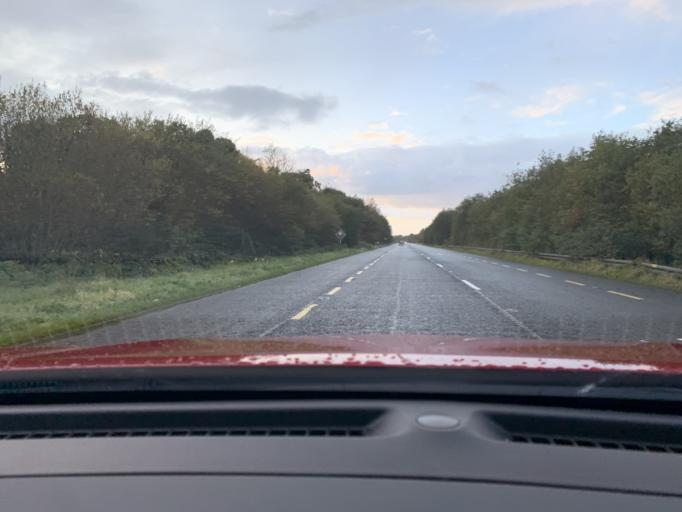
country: IE
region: Connaught
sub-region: County Leitrim
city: Carrick-on-Shannon
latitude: 53.9521
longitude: -8.1525
